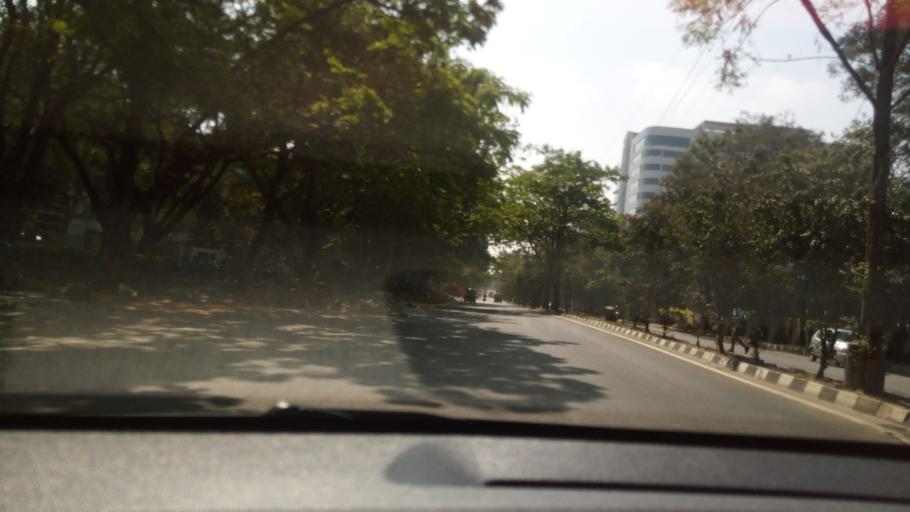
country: IN
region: Karnataka
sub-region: Bangalore Urban
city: Bangalore
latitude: 12.9760
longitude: 77.7105
